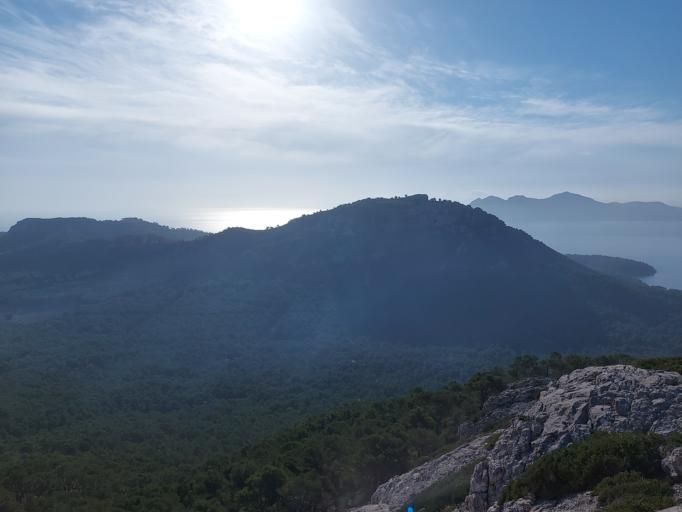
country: ES
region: Balearic Islands
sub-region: Illes Balears
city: Alcudia
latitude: 39.9439
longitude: 3.1386
